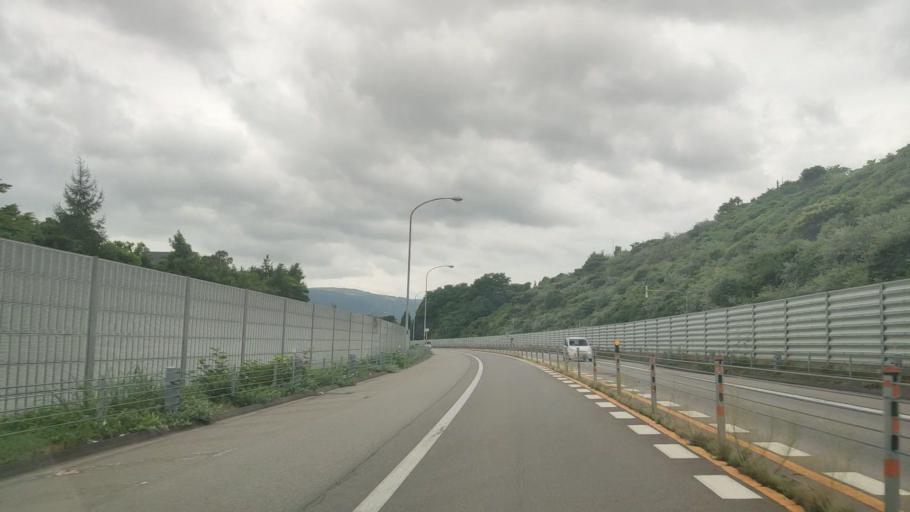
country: JP
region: Hokkaido
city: Nanae
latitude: 41.9143
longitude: 140.6900
